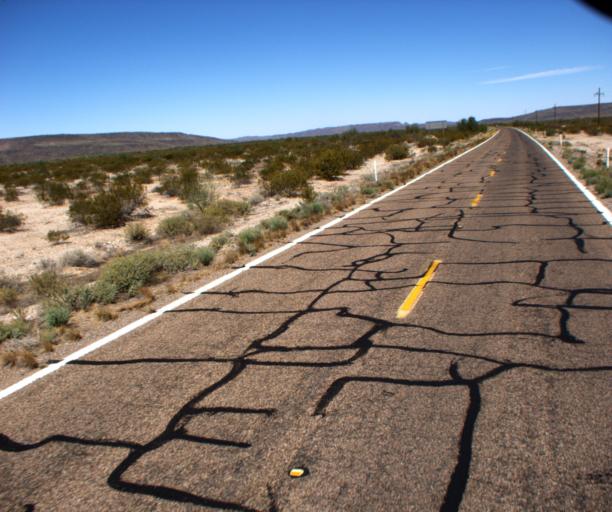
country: US
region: Arizona
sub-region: Pima County
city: Ajo
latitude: 32.4427
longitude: -112.8710
